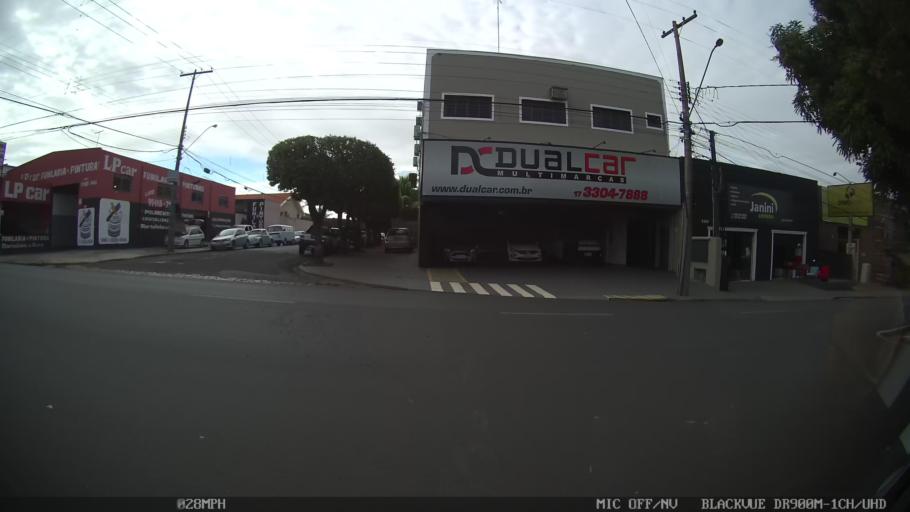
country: BR
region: Sao Paulo
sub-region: Sao Jose Do Rio Preto
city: Sao Jose do Rio Preto
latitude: -20.8352
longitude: -49.3713
